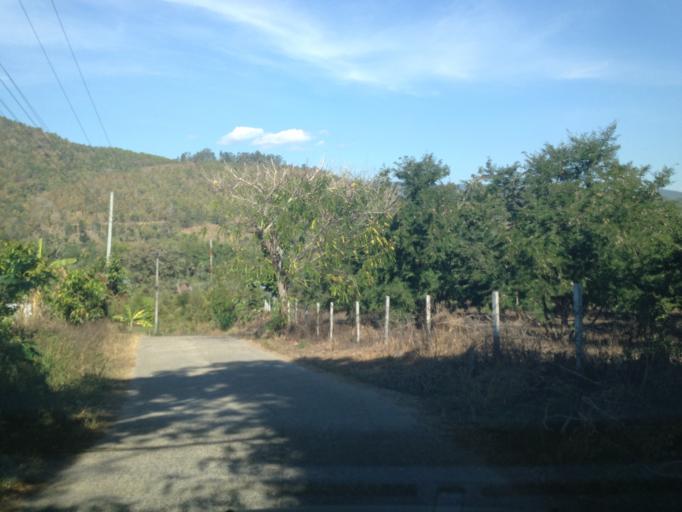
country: TH
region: Mae Hong Son
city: Ban Huai I Huak
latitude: 18.0872
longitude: 98.2028
